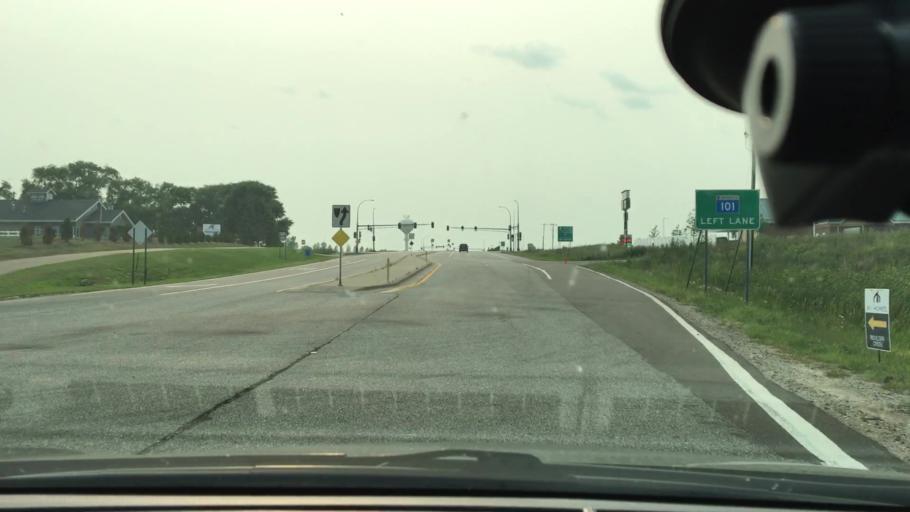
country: US
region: Minnesota
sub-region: Hennepin County
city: Dayton
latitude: 45.2524
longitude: -93.5506
